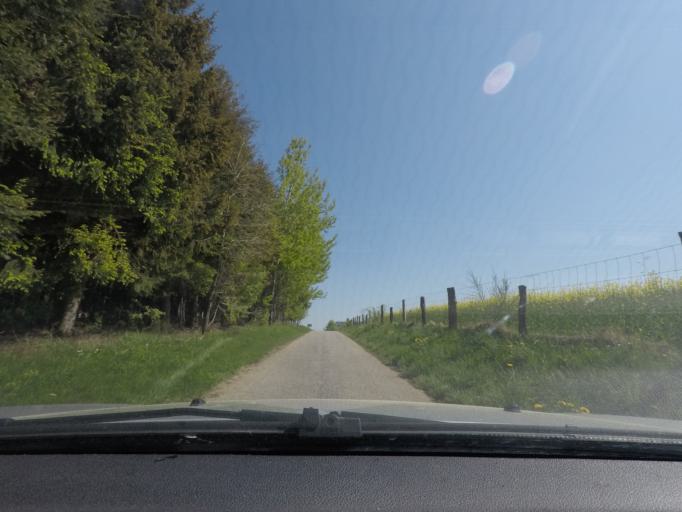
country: BE
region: Wallonia
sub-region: Province du Luxembourg
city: Leglise
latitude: 49.7871
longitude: 5.4812
